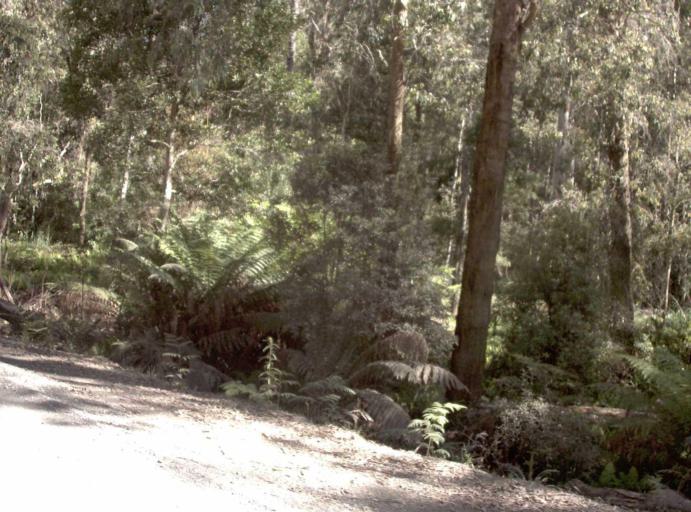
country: AU
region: New South Wales
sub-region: Bombala
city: Bombala
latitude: -37.2124
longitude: 148.7454
